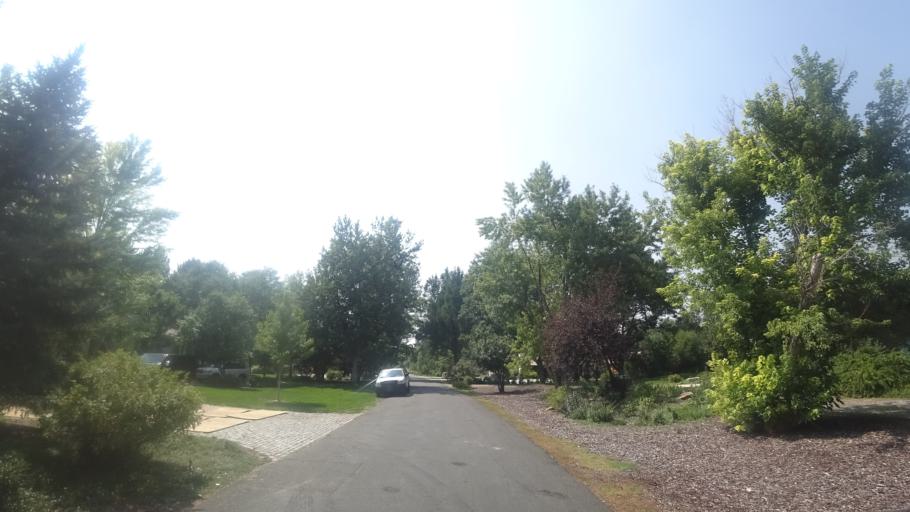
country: US
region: Colorado
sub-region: Arapahoe County
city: Cherry Hills Village
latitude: 39.6284
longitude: -104.9723
